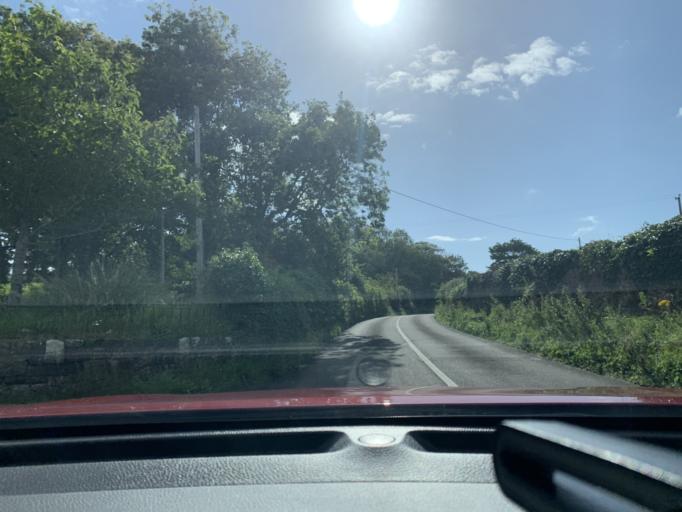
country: IE
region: Connaught
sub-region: Sligo
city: Strandhill
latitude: 54.3580
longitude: -8.5860
